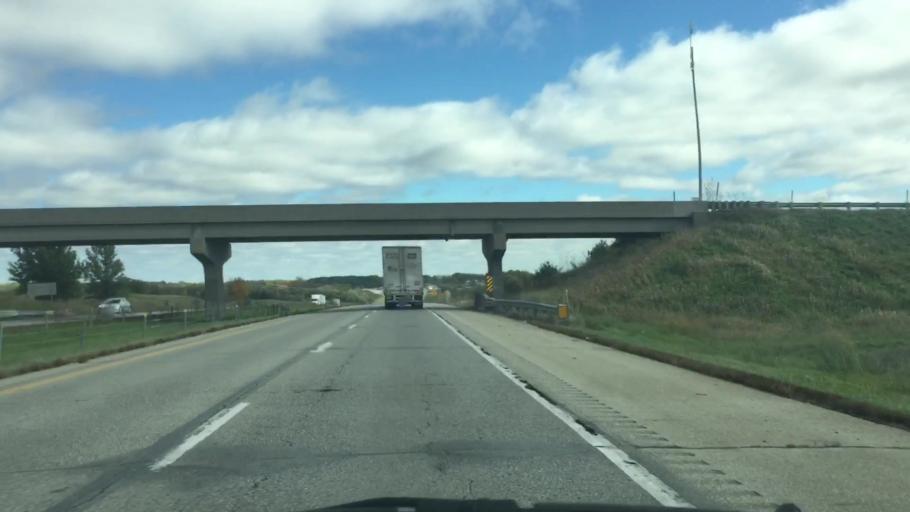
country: US
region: Iowa
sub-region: Poweshiek County
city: Grinnell
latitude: 41.6950
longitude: -92.7950
